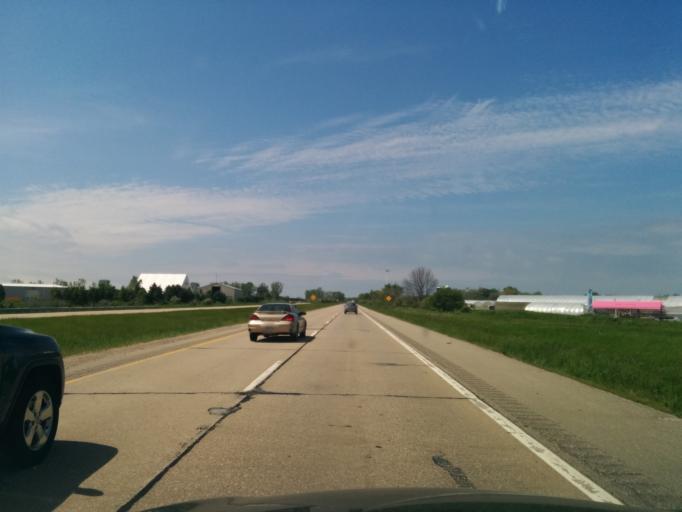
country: US
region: Michigan
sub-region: Ottawa County
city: Holland
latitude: 42.7394
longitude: -86.1364
